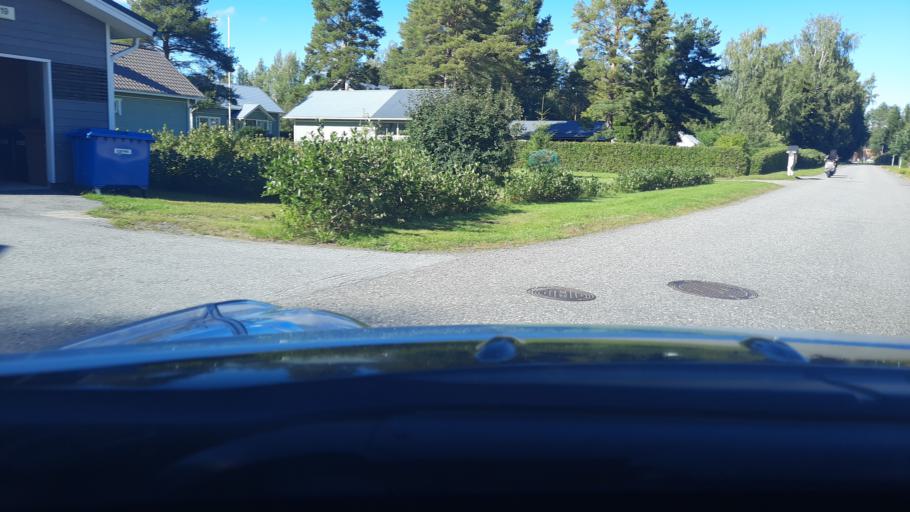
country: FI
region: North Karelia
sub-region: Joensuu
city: Joensuu
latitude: 62.6353
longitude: 29.6842
